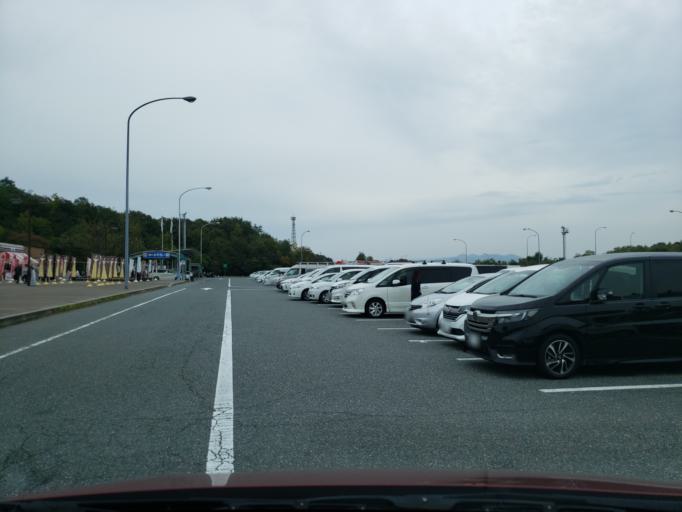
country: JP
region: Hyogo
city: Miki
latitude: 34.8174
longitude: 134.9800
